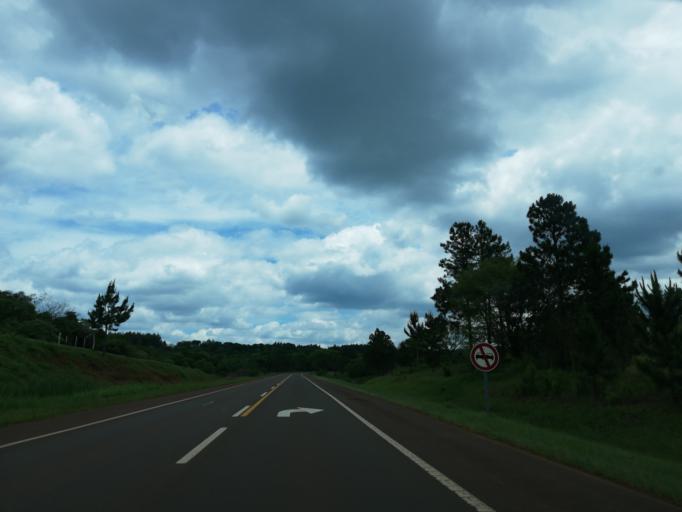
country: AR
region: Misiones
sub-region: Departamento de Leandro N. Alem
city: Leandro N. Alem
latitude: -27.6443
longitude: -55.3535
